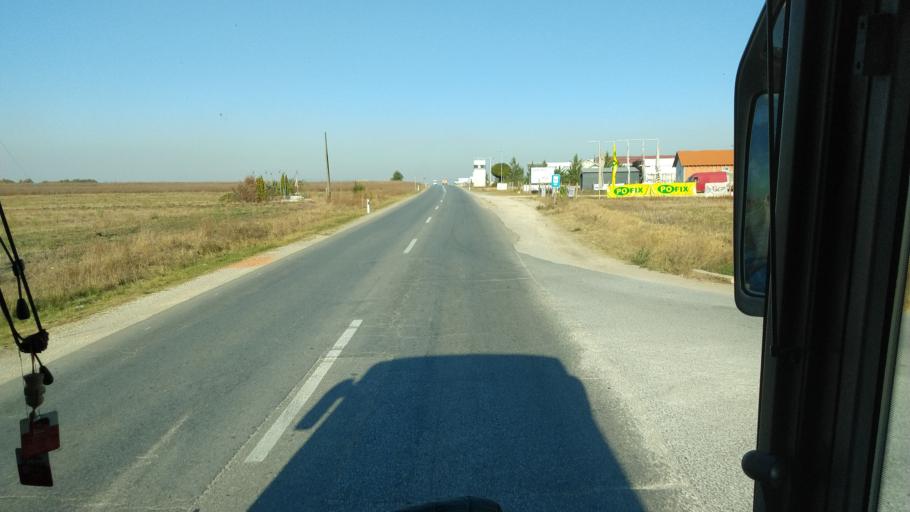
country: XK
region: Pristina
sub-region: Lipjan
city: Lipljan
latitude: 42.4890
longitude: 21.0952
